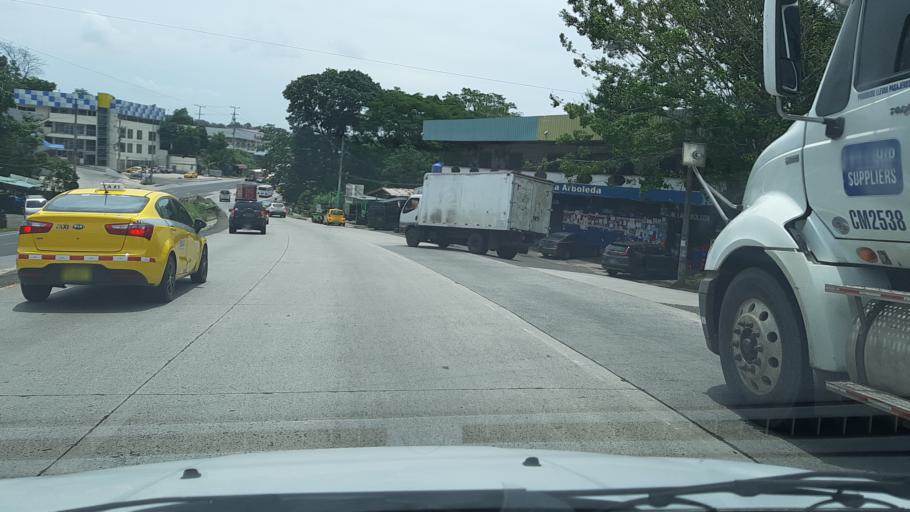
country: PA
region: Panama
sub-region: Distrito Arraijan
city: Arraijan
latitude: 8.9488
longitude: -79.6709
